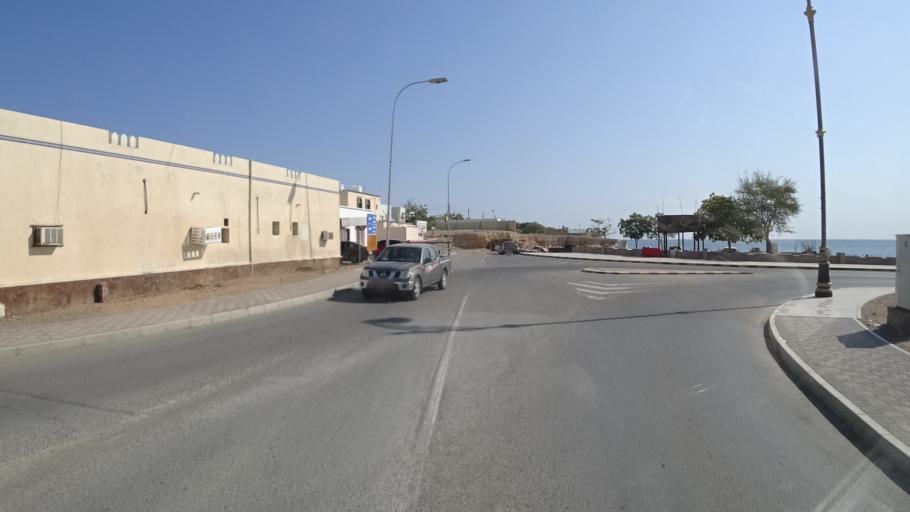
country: OM
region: Ash Sharqiyah
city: Sur
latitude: 22.5729
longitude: 59.5274
